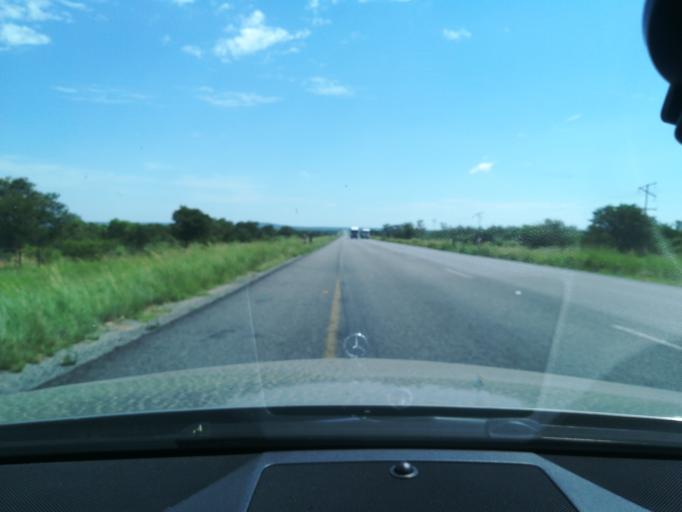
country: ZA
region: North-West
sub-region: Dr Kenneth Kaunda District Municipality
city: Wolmaransstad
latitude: -27.0060
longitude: 26.1946
